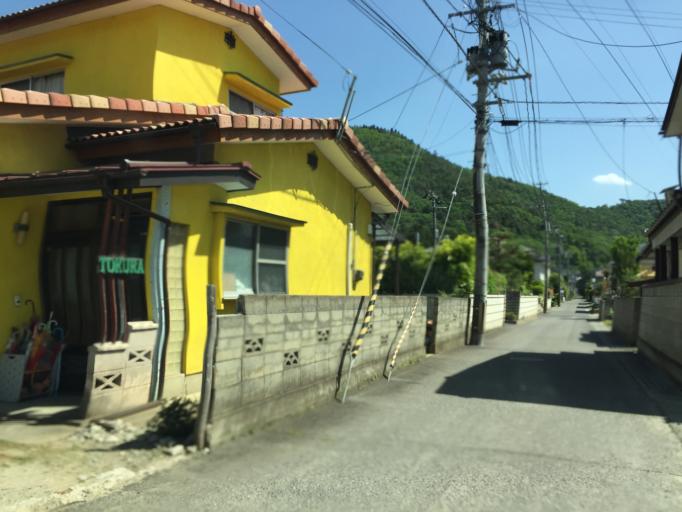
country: JP
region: Fukushima
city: Fukushima-shi
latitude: 37.7807
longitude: 140.4692
